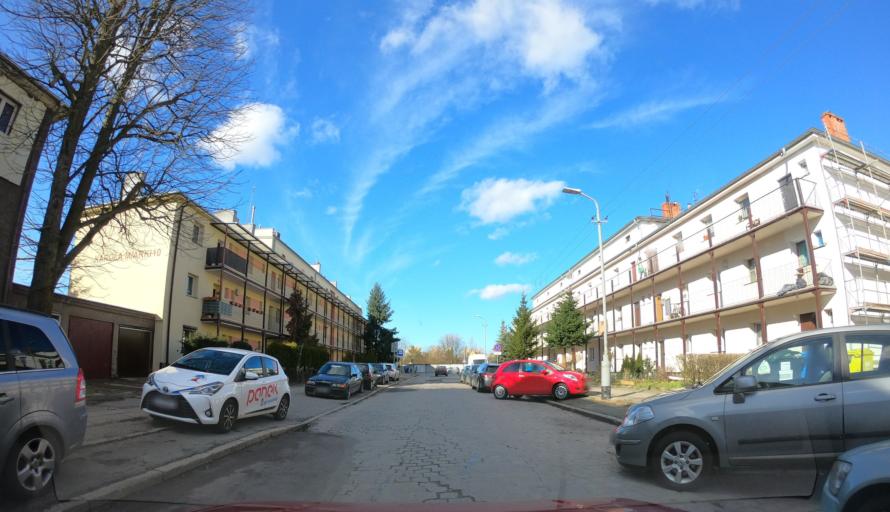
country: PL
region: West Pomeranian Voivodeship
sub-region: Szczecin
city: Szczecin
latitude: 53.4230
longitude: 14.5147
